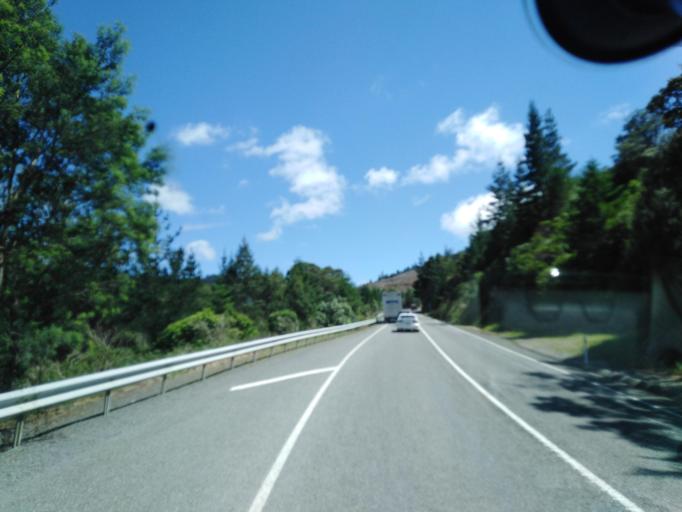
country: NZ
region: Nelson
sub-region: Nelson City
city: Nelson
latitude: -41.1968
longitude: 173.5584
